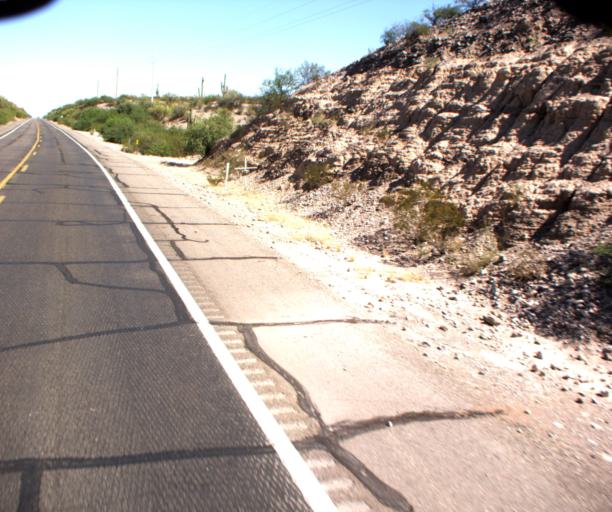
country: US
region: Arizona
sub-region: Pinal County
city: Mammoth
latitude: 32.7538
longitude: -110.6475
